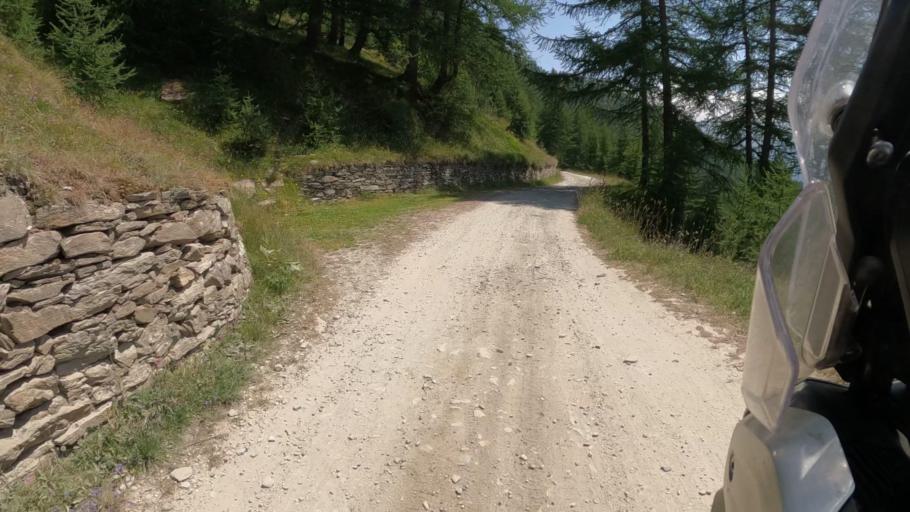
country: IT
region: Piedmont
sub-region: Provincia di Torino
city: Fenestrelle
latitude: 45.0570
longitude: 7.0506
